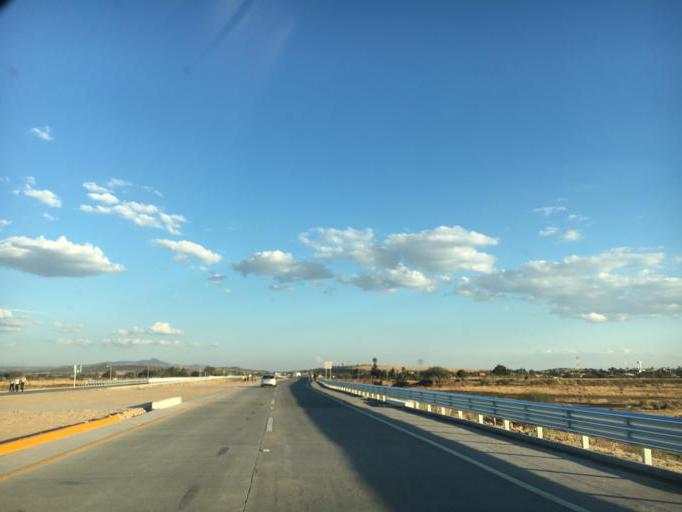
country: MX
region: Guanajuato
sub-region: Leon
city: Ladrilleras del Refugio
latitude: 21.0817
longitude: -101.5522
